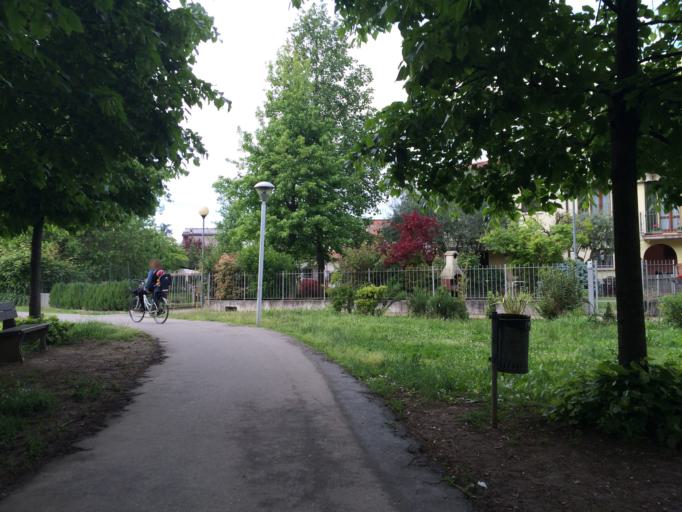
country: IT
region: Lombardy
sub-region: Provincia di Brescia
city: Flero
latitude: 45.4821
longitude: 10.1750
